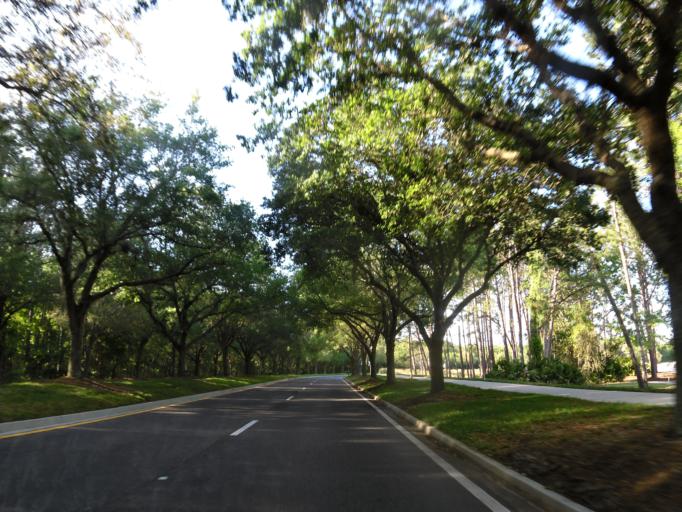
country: US
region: Florida
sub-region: Saint Johns County
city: Villano Beach
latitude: 29.9904
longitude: -81.4764
